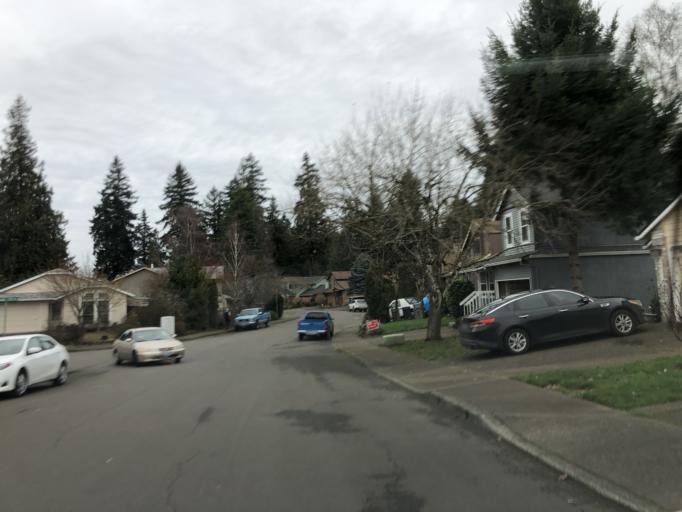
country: US
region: Oregon
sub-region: Washington County
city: Tigard
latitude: 45.4164
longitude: -122.7628
